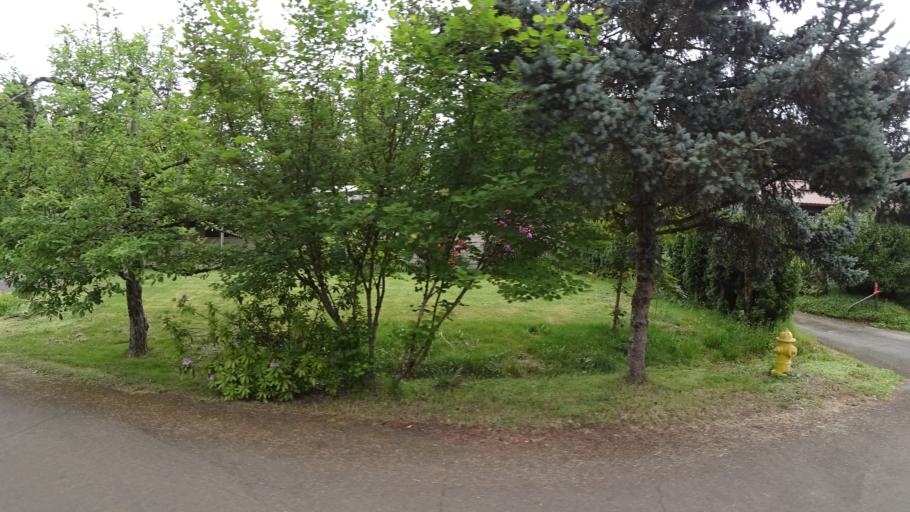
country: US
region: Oregon
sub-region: Washington County
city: Garden Home-Whitford
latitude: 45.4690
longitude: -122.7553
